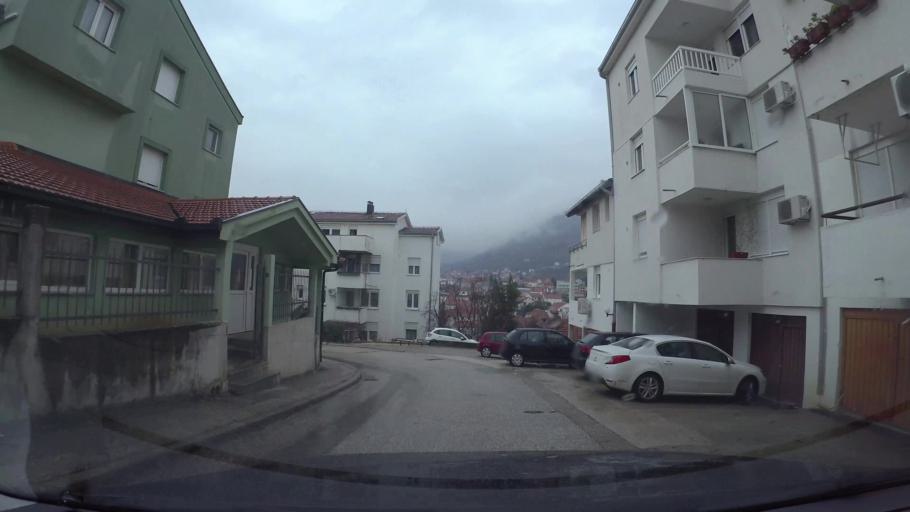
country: BA
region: Federation of Bosnia and Herzegovina
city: Cim
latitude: 43.3476
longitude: 17.7915
